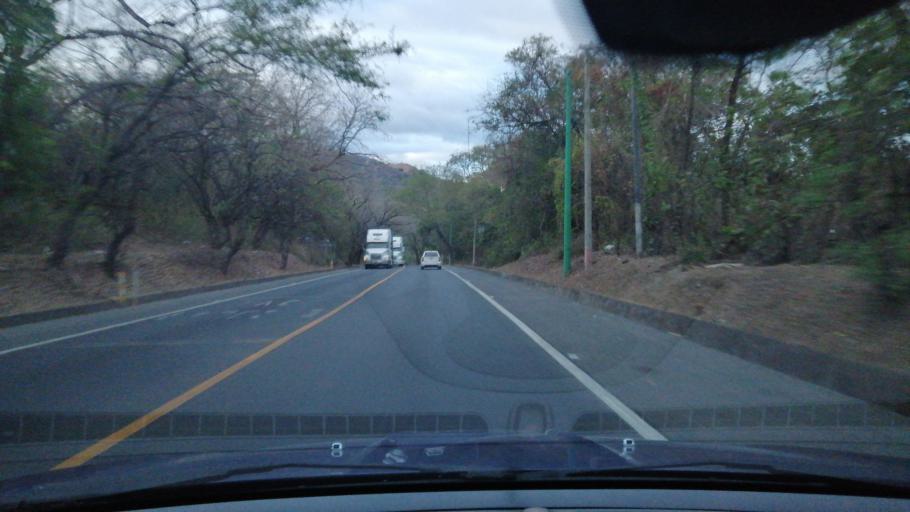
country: SV
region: Santa Ana
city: Santa Ana
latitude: 14.0059
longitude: -89.5420
